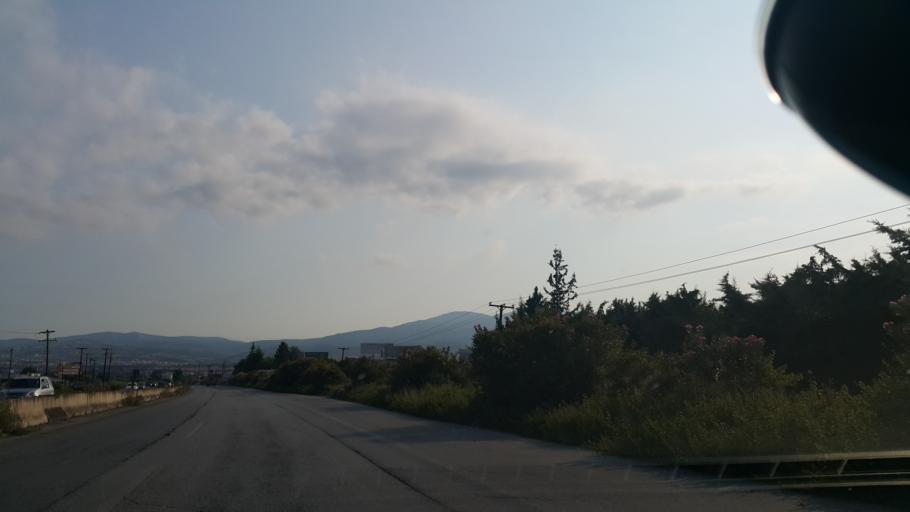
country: GR
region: Central Macedonia
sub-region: Nomos Thessalonikis
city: Neo Rysi
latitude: 40.4996
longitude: 23.0042
